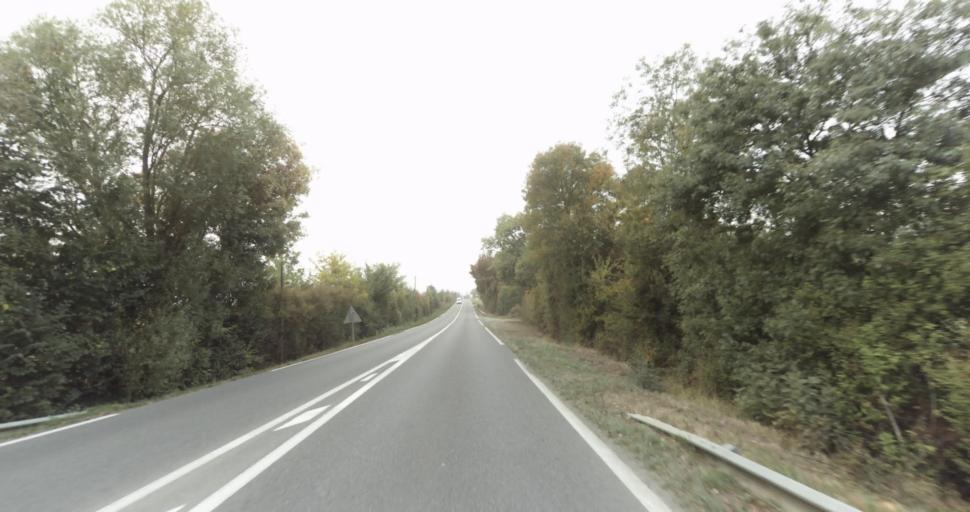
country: FR
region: Midi-Pyrenees
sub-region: Departement du Gers
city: Preignan
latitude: 43.7048
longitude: 0.6177
